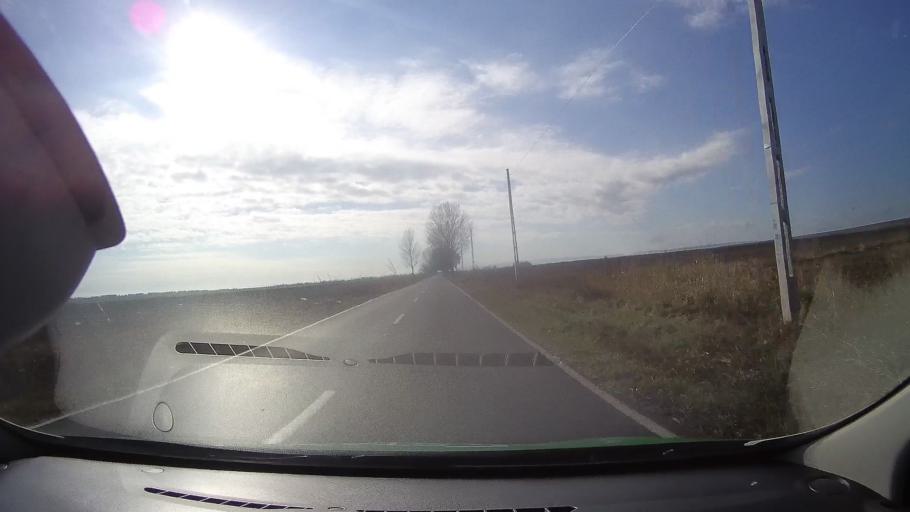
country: RO
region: Tulcea
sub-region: Comuna Valea Nucarilor
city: Agighiol
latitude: 44.9939
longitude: 28.8862
